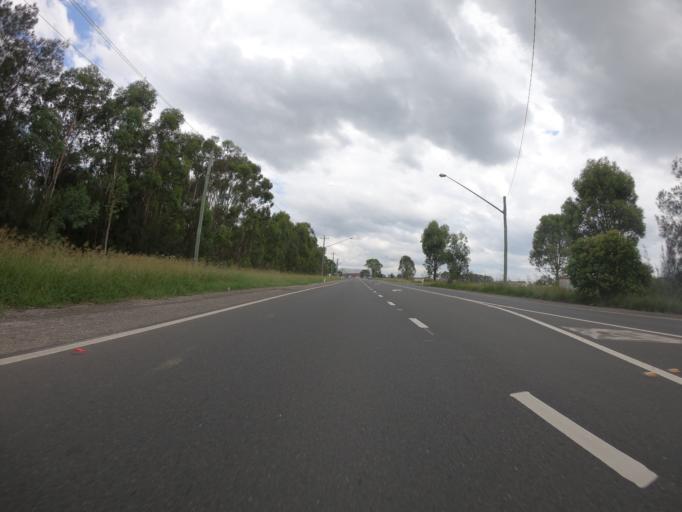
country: AU
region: New South Wales
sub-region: Blacktown
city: Mount Druitt
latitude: -33.8149
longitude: 150.7759
